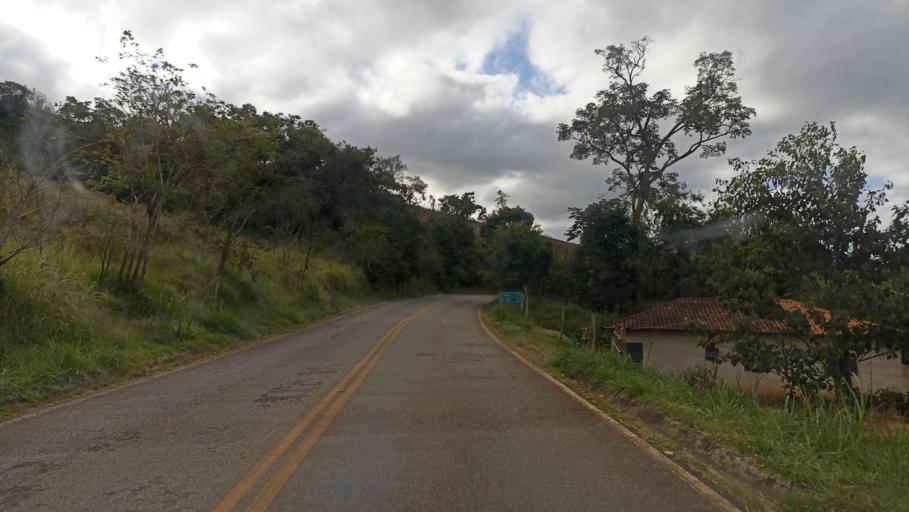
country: BR
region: Minas Gerais
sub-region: Tiradentes
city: Tiradentes
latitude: -21.0807
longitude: -44.0748
